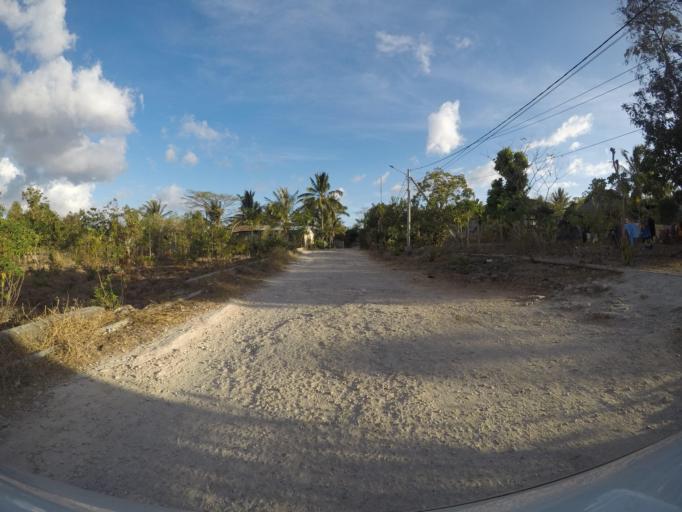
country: TL
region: Baucau
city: Baucau
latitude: -8.4752
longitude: 126.4538
